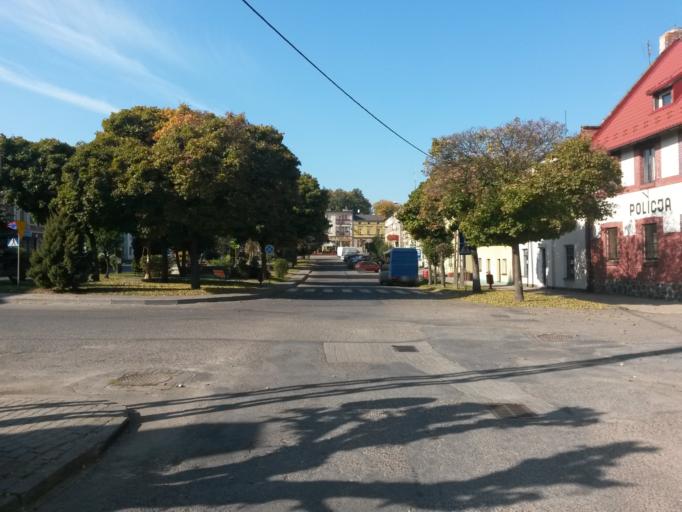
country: PL
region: Kujawsko-Pomorskie
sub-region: Powiat brodnicki
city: Gorzno
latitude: 53.1977
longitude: 19.6457
